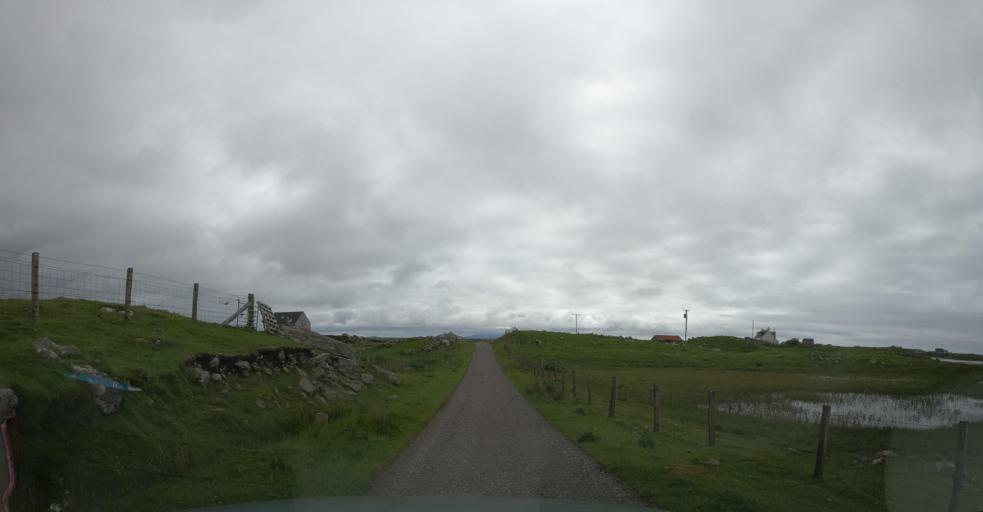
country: GB
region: Scotland
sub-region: Eilean Siar
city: Isle of North Uist
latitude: 57.5462
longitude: -7.3447
